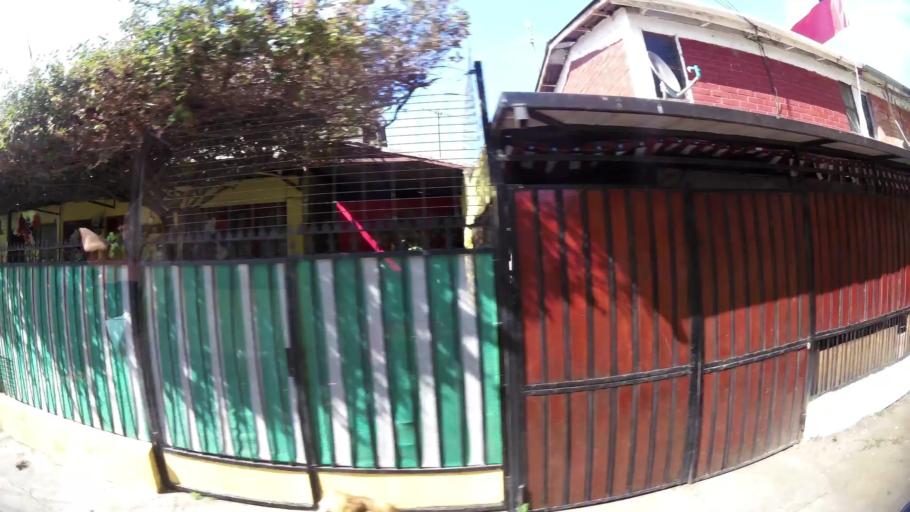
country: CL
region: Santiago Metropolitan
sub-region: Provincia de Talagante
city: Talagante
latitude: -33.6779
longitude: -70.9490
